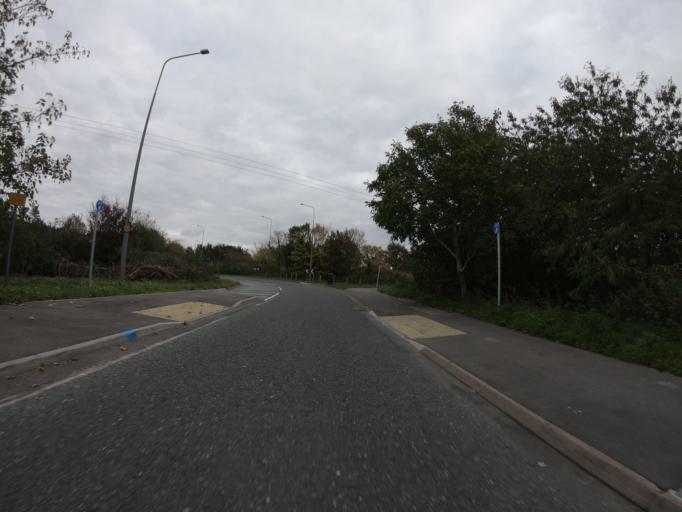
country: GB
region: England
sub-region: Borough of Thurrock
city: Chadwell St Mary
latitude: 51.4774
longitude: 0.3472
